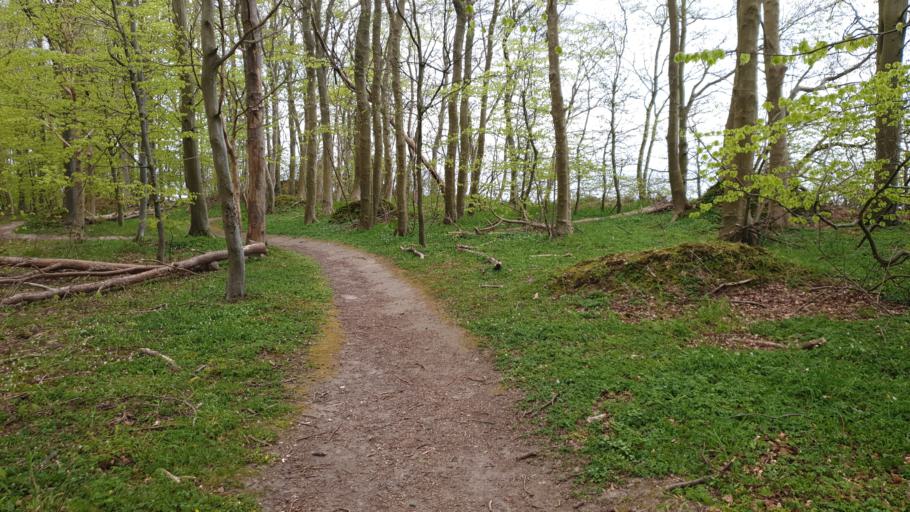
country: DK
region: South Denmark
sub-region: Sonderborg Kommune
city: Dybbol
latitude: 54.8498
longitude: 9.7605
